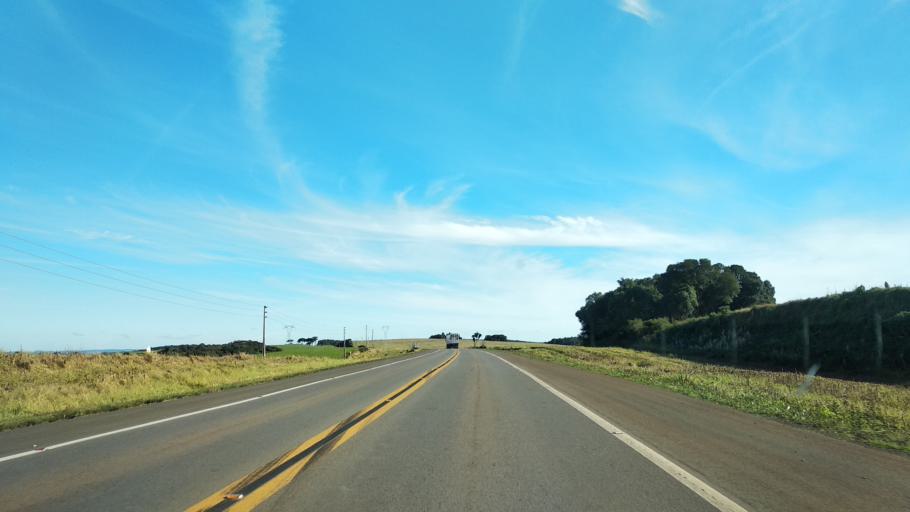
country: BR
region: Santa Catarina
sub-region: Celso Ramos
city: Celso Ramos
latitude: -27.4965
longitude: -51.3390
